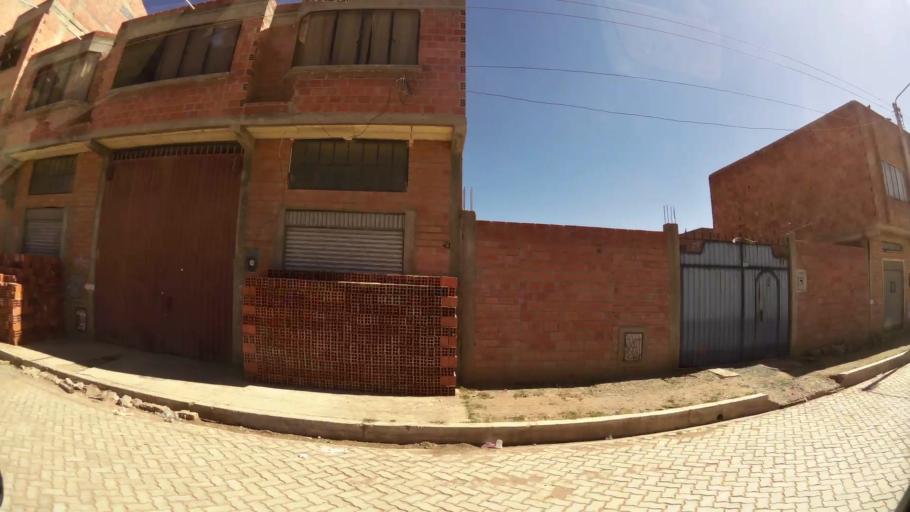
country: BO
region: La Paz
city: La Paz
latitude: -16.5388
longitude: -68.1959
